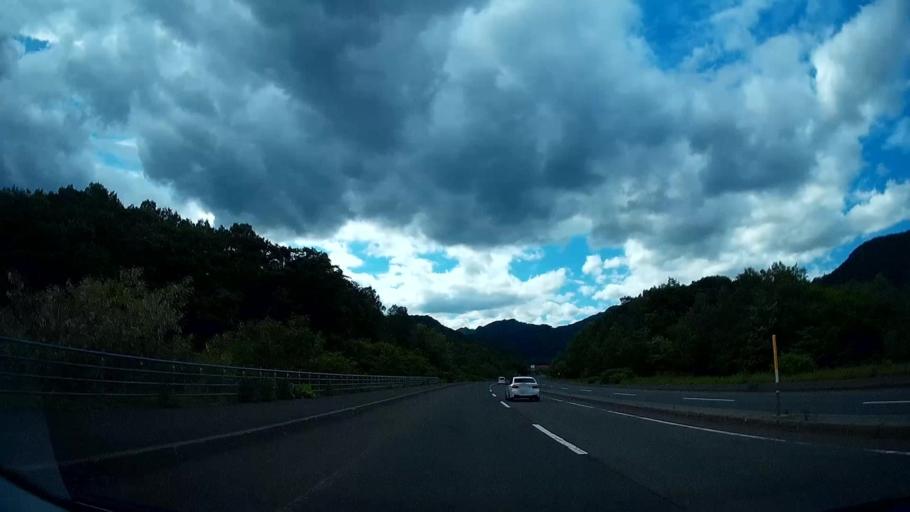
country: JP
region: Hokkaido
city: Sapporo
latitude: 42.9584
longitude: 141.2284
